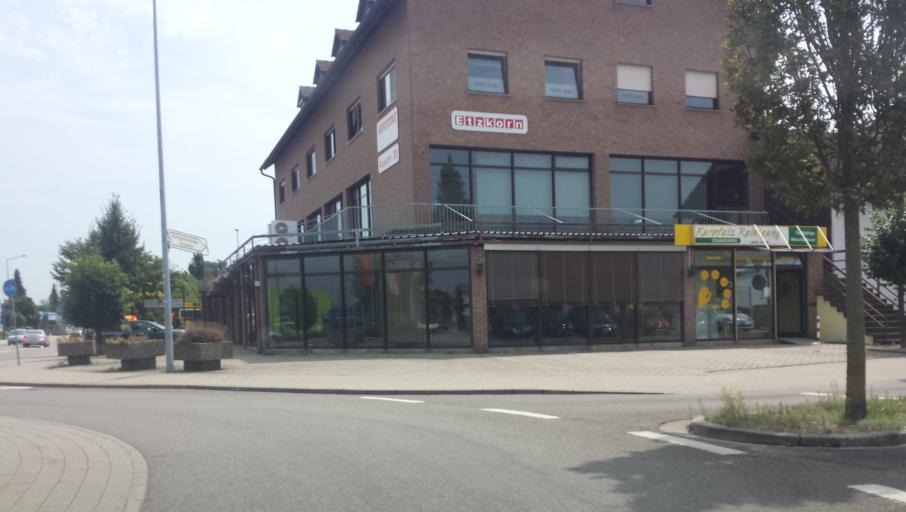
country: DE
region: Rheinland-Pfalz
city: Speyer
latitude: 49.3343
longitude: 8.4364
